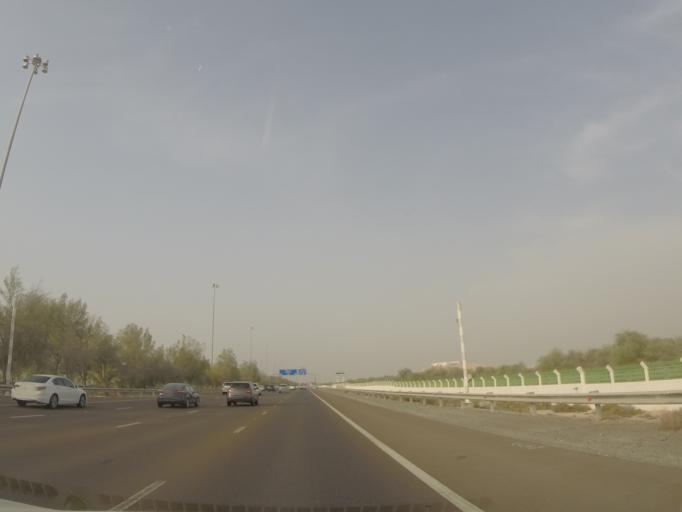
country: AE
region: Dubai
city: Dubai
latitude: 24.7212
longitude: 54.8079
